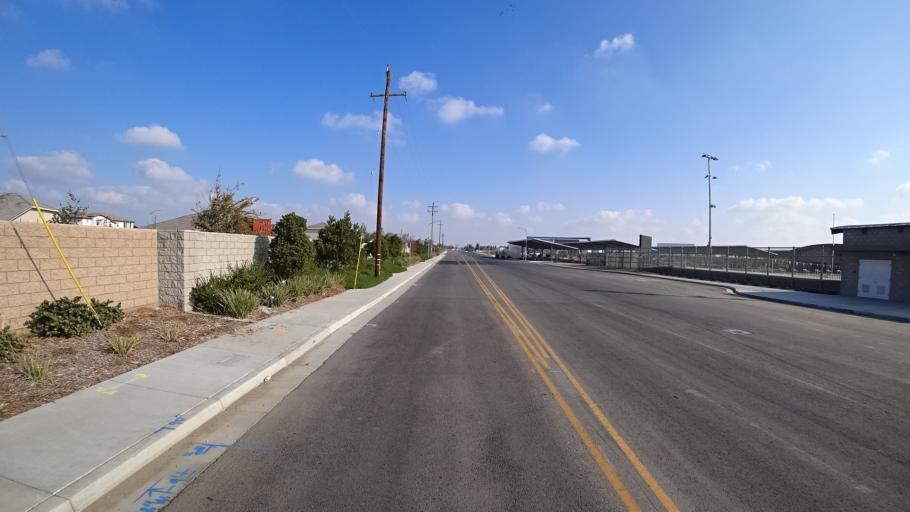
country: US
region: California
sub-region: Kern County
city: Greenacres
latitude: 35.2890
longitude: -119.1144
